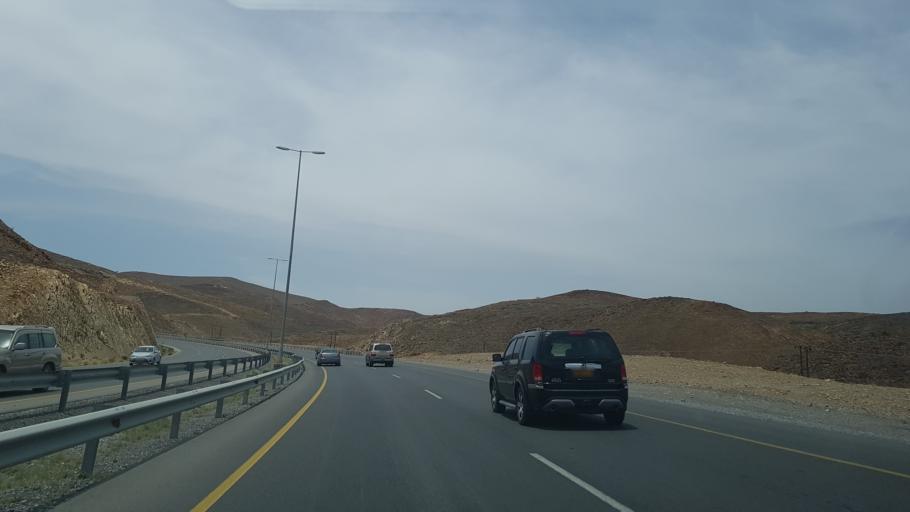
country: OM
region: Muhafazat ad Dakhiliyah
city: Izki
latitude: 22.8996
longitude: 57.7238
